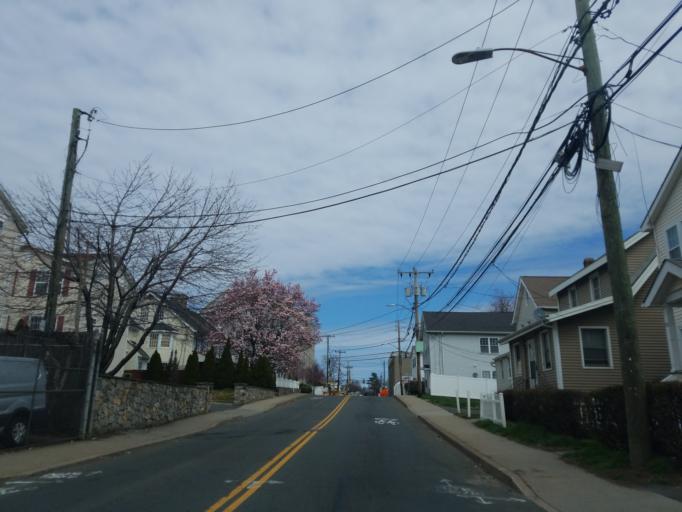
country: US
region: Connecticut
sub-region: Fairfield County
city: Stamford
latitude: 41.0470
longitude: -73.5581
